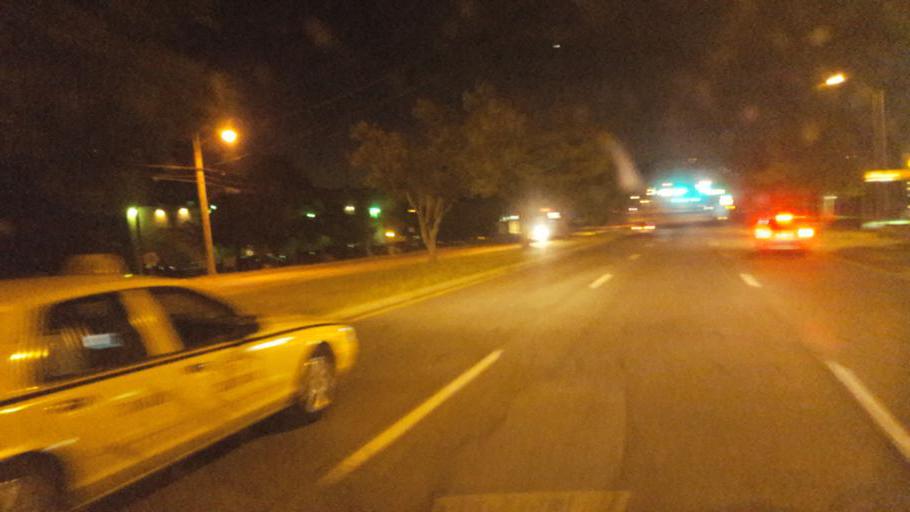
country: US
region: Virginia
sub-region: Fairfax County
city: Lincolnia
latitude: 38.8124
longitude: -77.1230
